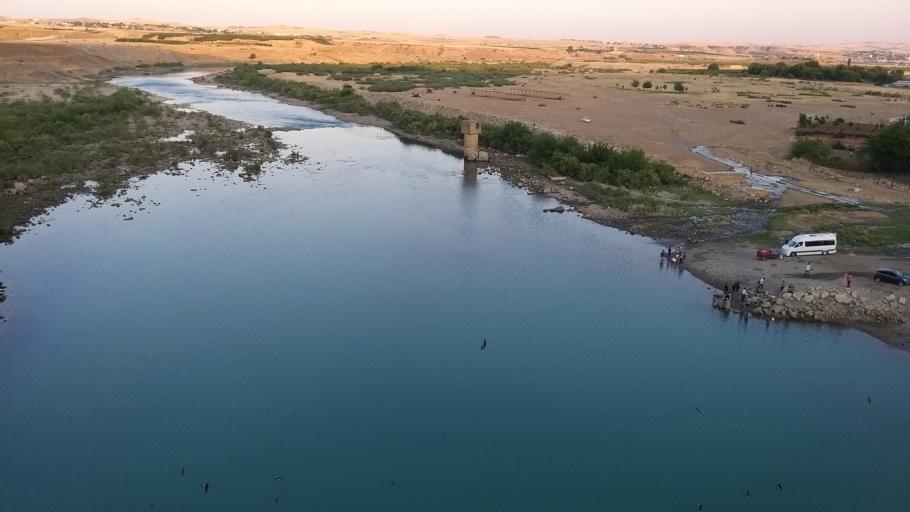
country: TR
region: Diyarbakir
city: Malabadi
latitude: 38.1537
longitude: 41.2039
